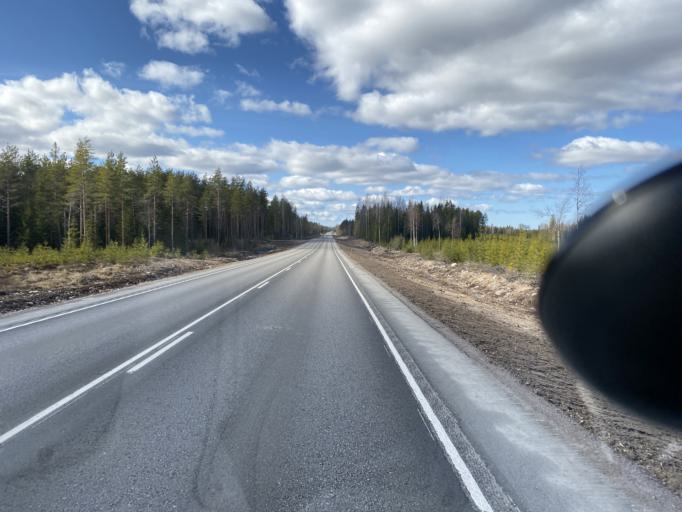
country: FI
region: Satakunta
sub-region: Pori
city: Kokemaeki
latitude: 61.1693
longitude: 22.4595
